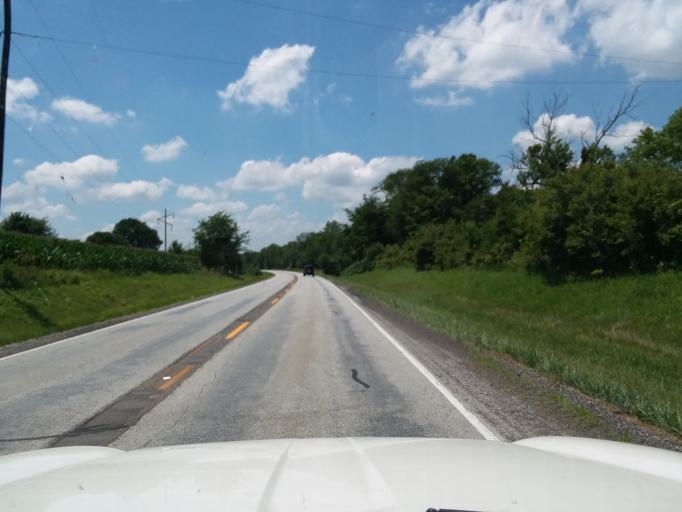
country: US
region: Indiana
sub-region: Johnson County
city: Trafalgar
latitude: 39.4077
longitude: -86.1758
